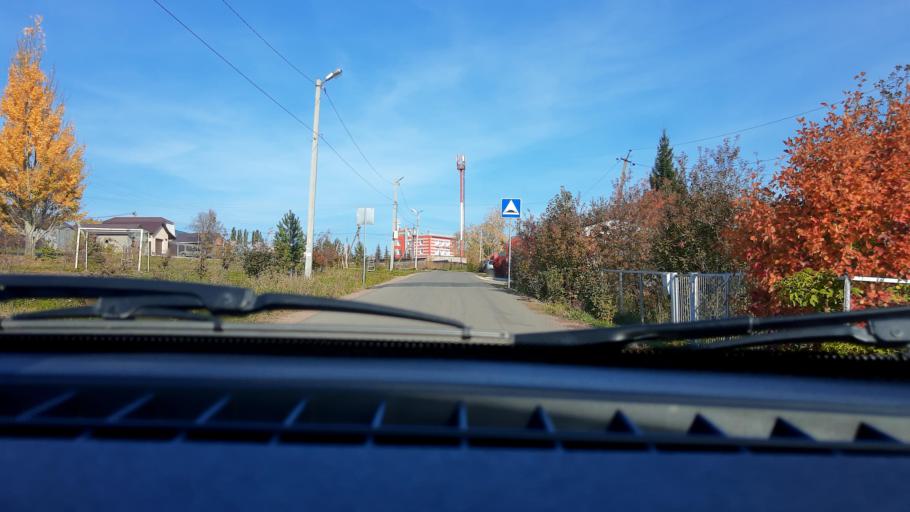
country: RU
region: Bashkortostan
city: Mikhaylovka
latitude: 54.8118
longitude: 55.8932
